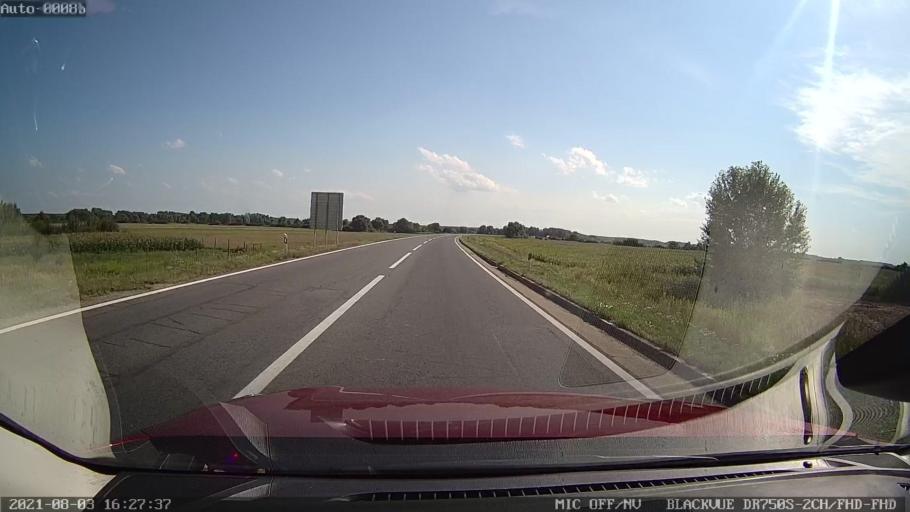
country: HR
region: Osjecko-Baranjska
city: Darda
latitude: 45.6187
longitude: 18.6758
